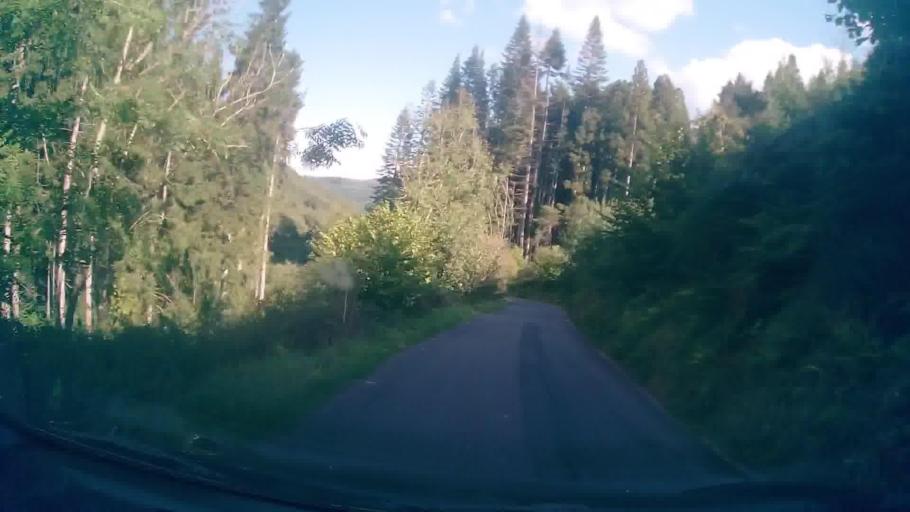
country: GB
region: Wales
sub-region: Merthyr Tydfil County Borough
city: Merthyr Tydfil
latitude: 51.8437
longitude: -3.3638
